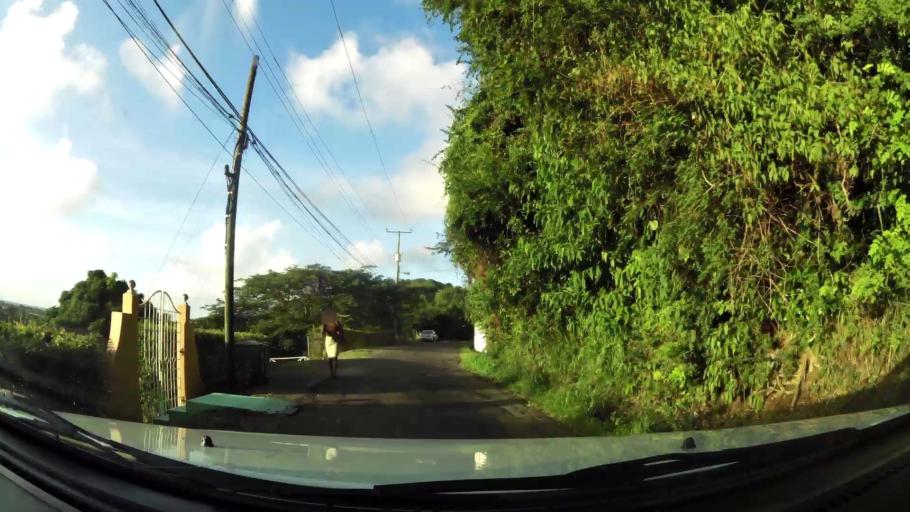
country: LC
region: Gros-Islet
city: Gros Islet
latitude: 14.0661
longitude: -60.9421
